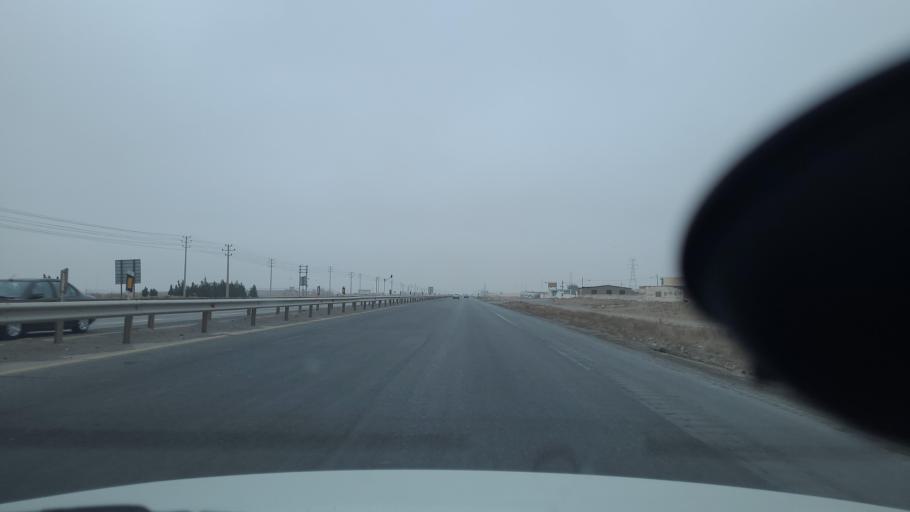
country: IR
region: Razavi Khorasan
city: Fariman
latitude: 35.9344
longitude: 59.7515
